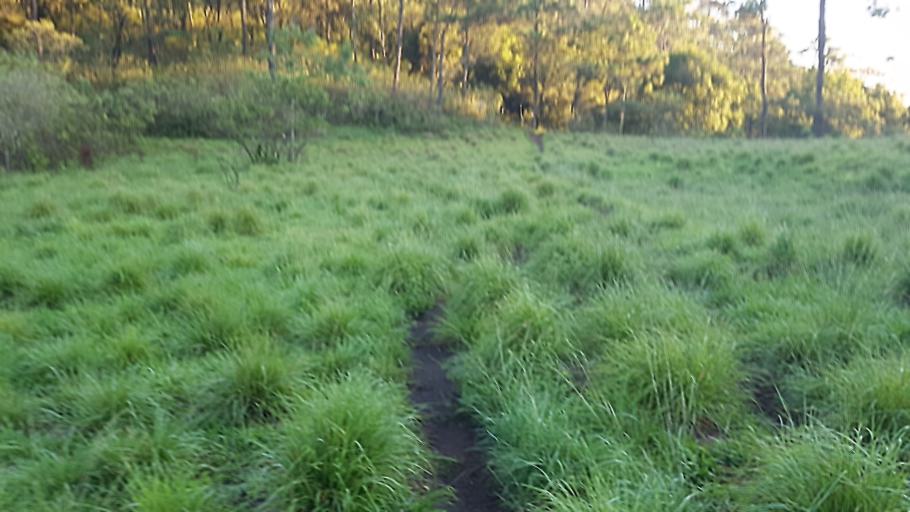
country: MX
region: Nayarit
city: Tepic
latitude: 21.5015
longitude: -104.9307
